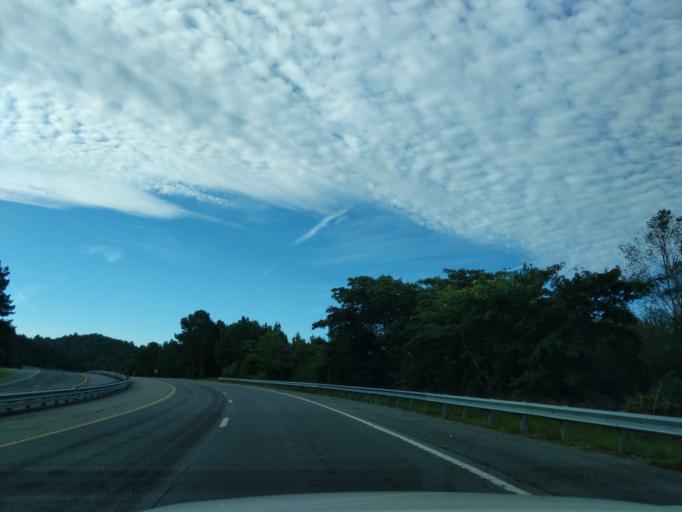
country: US
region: Georgia
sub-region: Fannin County
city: McCaysville
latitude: 35.0209
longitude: -84.3839
